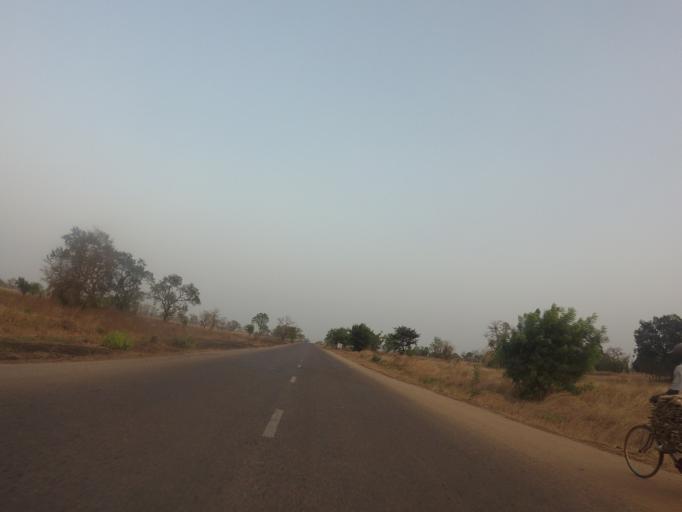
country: GH
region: Northern
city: Tamale
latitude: 9.4402
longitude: -1.0999
